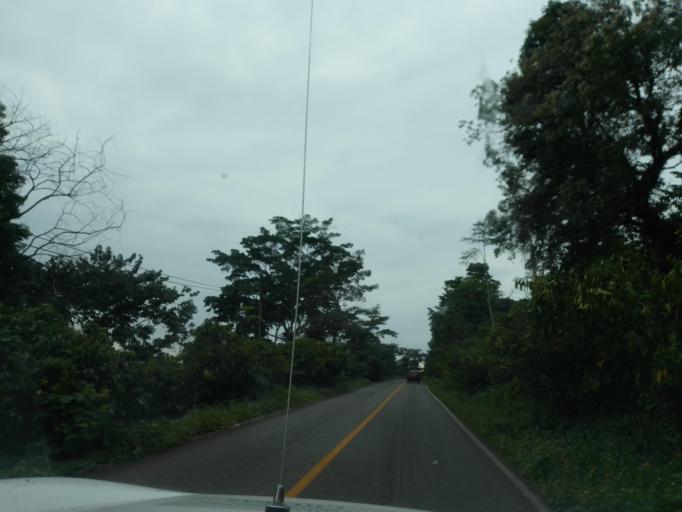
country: MX
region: Chiapas
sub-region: Union Juarez
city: Santo Domingo
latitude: 15.0386
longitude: -92.1269
